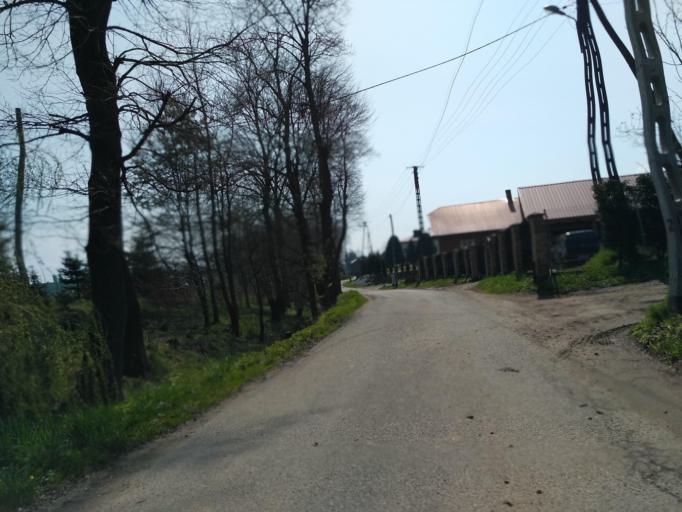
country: PL
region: Subcarpathian Voivodeship
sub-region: Powiat sanocki
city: Zarszyn
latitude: 49.6168
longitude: 22.0110
